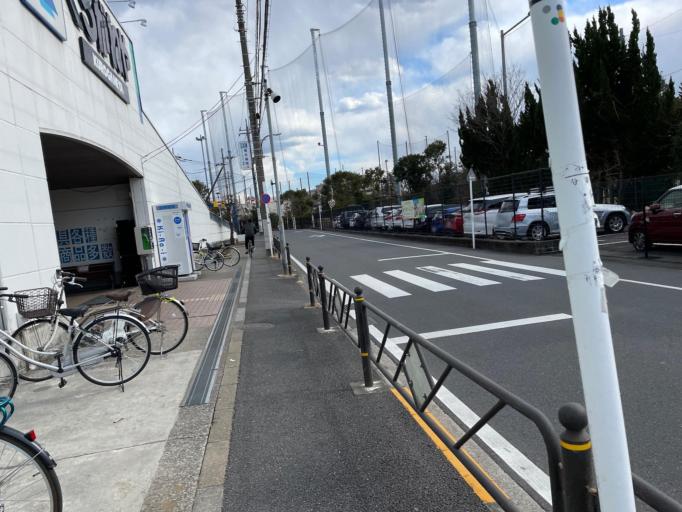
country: JP
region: Tokyo
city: Chofugaoka
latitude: 35.6491
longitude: 139.5273
